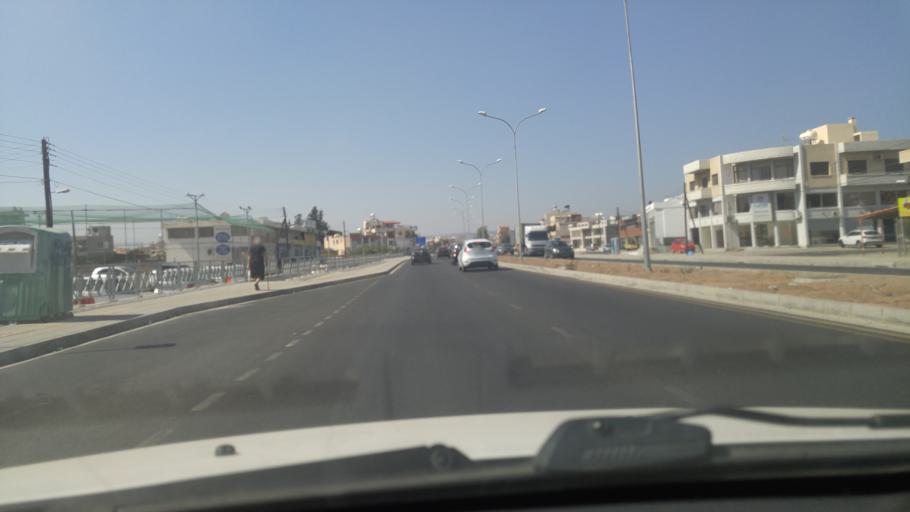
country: CY
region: Limassol
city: Pano Polemidia
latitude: 34.6789
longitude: 32.9948
